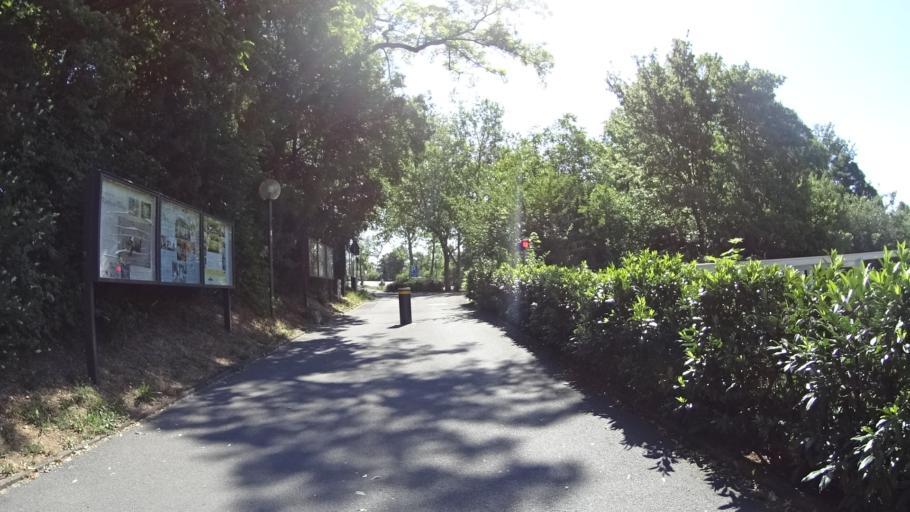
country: DE
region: Baden-Wuerttemberg
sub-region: Regierungsbezirk Stuttgart
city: Bad Mergentheim
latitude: 49.4936
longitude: 9.7883
